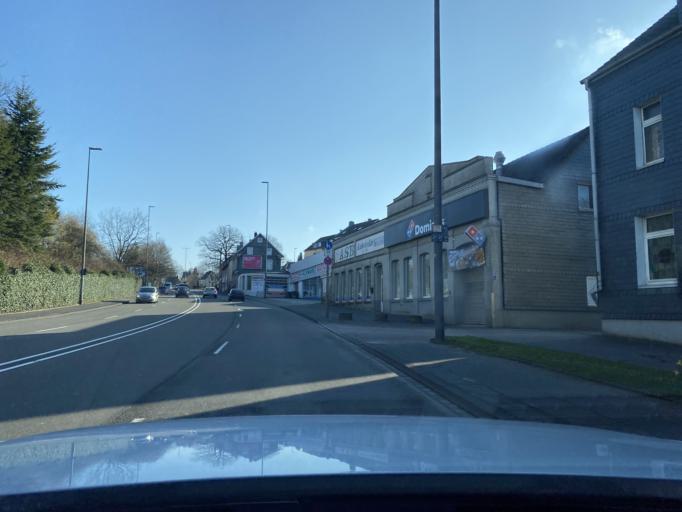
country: DE
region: North Rhine-Westphalia
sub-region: Regierungsbezirk Dusseldorf
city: Remscheid
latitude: 51.1773
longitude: 7.2192
